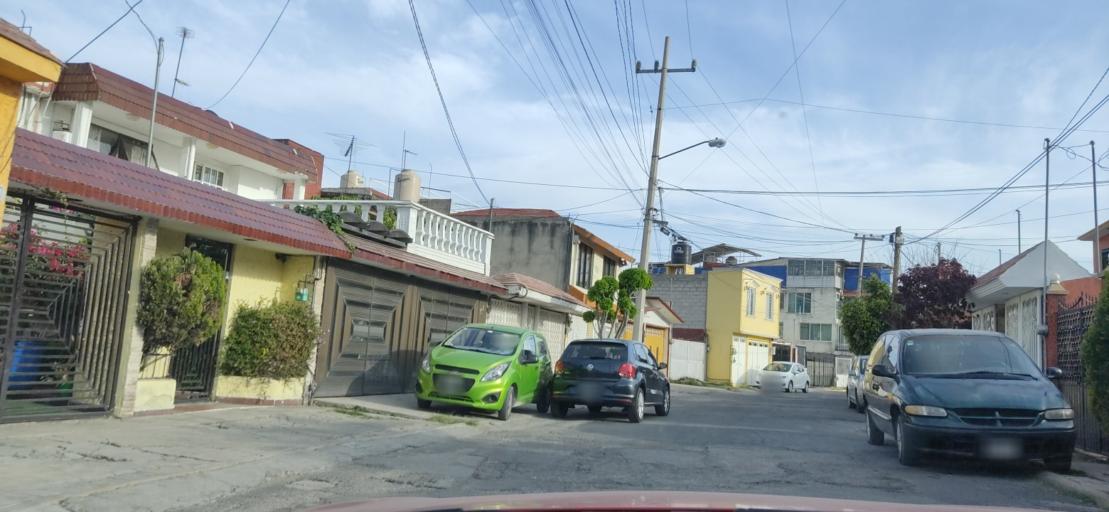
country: MX
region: Mexico
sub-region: Cuautitlan
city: San Jose del Puente
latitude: 19.6913
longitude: -99.2054
